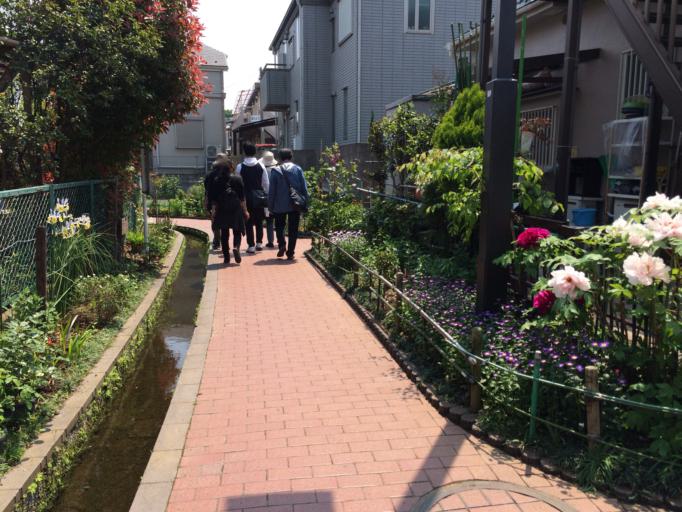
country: JP
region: Kanagawa
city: Yokohama
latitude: 35.5079
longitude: 139.6443
